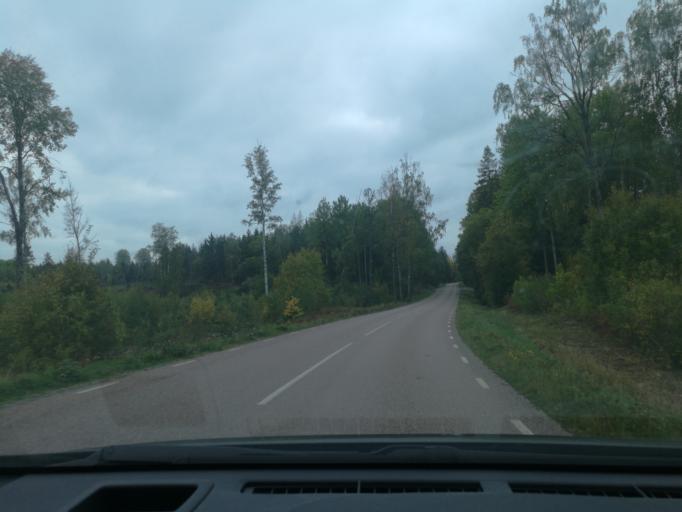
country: SE
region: Vaestmanland
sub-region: Vasteras
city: Tillberga
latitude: 59.7219
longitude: 16.6679
